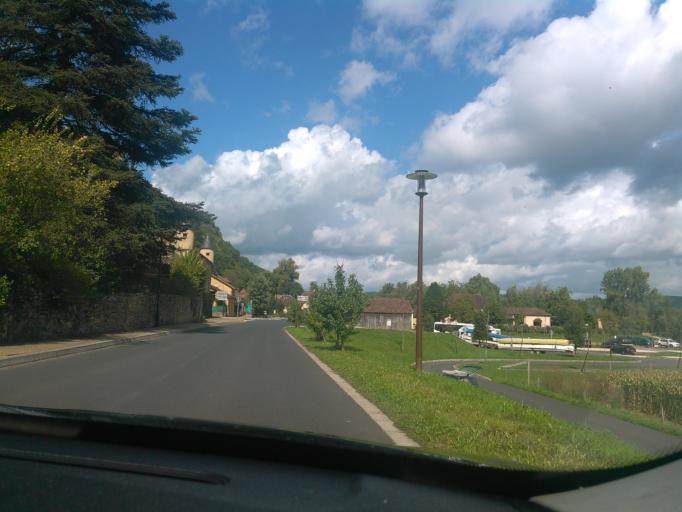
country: FR
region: Aquitaine
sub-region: Departement de la Dordogne
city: Cenac-et-Saint-Julien
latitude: 44.8120
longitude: 1.1524
